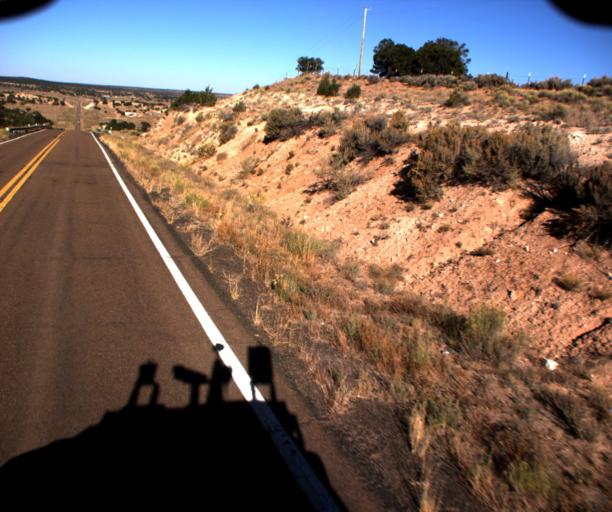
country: US
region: Arizona
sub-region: Apache County
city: Ganado
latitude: 35.7589
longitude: -109.9632
